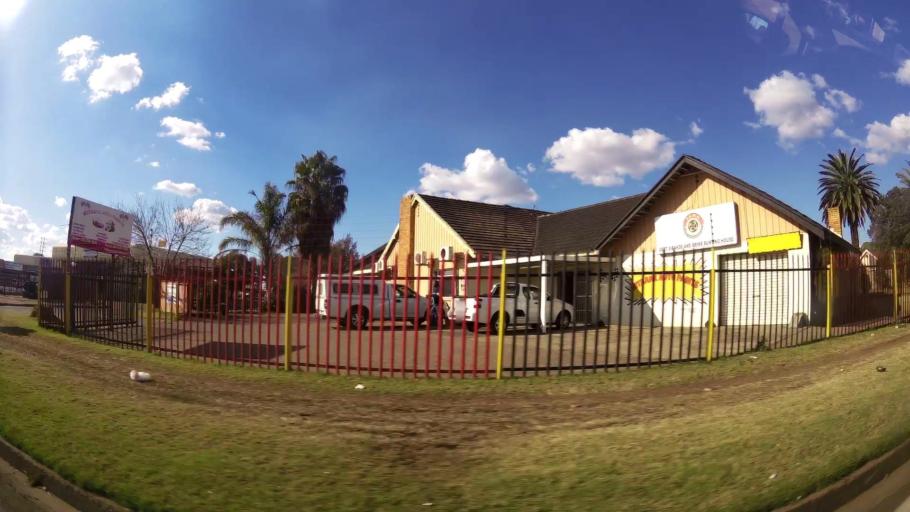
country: ZA
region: Mpumalanga
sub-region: Nkangala District Municipality
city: Witbank
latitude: -25.8887
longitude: 29.2235
